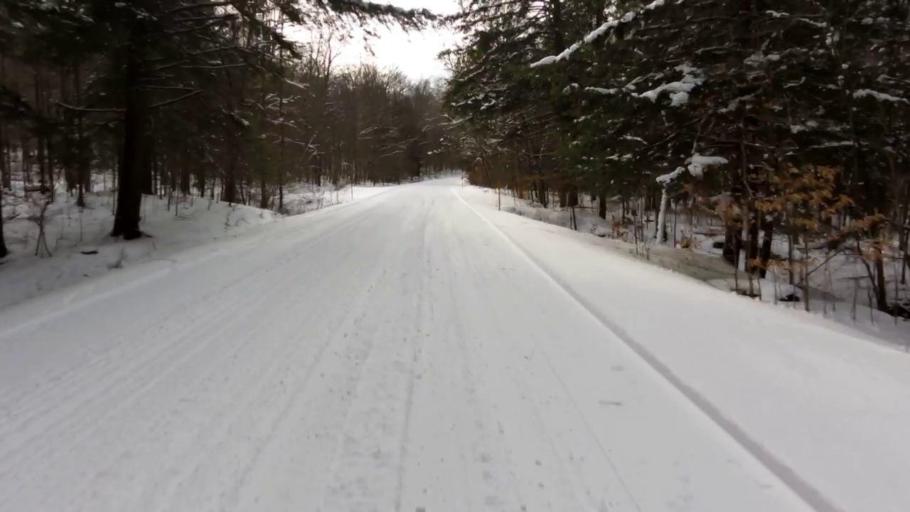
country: US
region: New York
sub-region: Cattaraugus County
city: Salamanca
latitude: 42.0794
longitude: -78.7498
